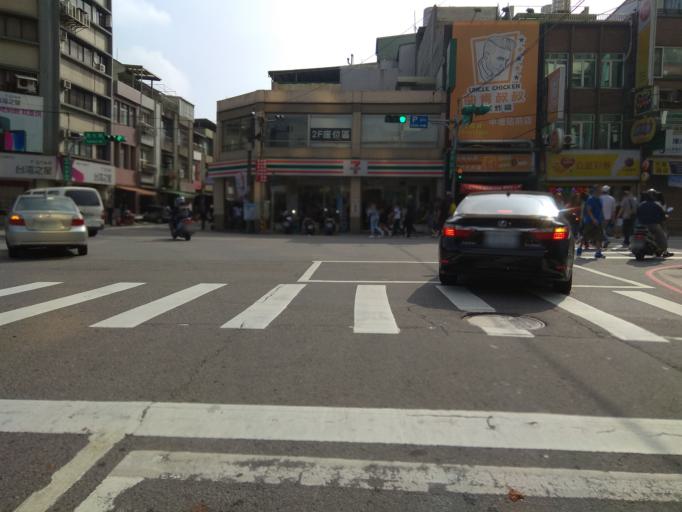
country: TW
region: Taiwan
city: Taoyuan City
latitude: 24.9560
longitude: 121.2268
